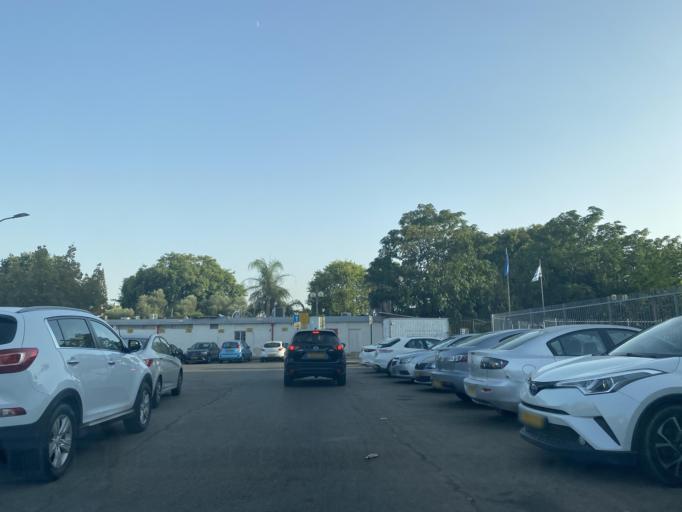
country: IL
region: Central District
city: Hod HaSharon
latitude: 32.1561
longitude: 34.9021
